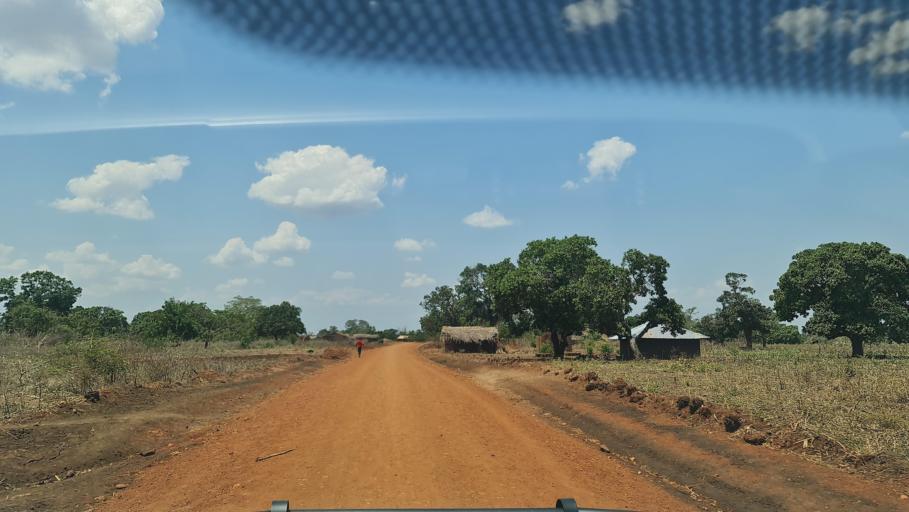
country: MZ
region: Nampula
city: Nacala
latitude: -14.8062
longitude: 40.0714
